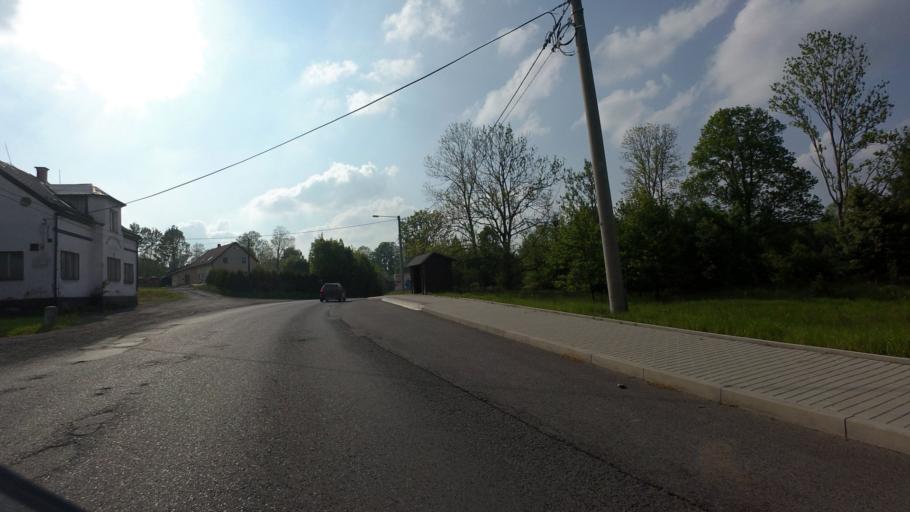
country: CZ
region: Ustecky
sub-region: Okres Decin
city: Sluknov
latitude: 51.0026
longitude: 14.4327
